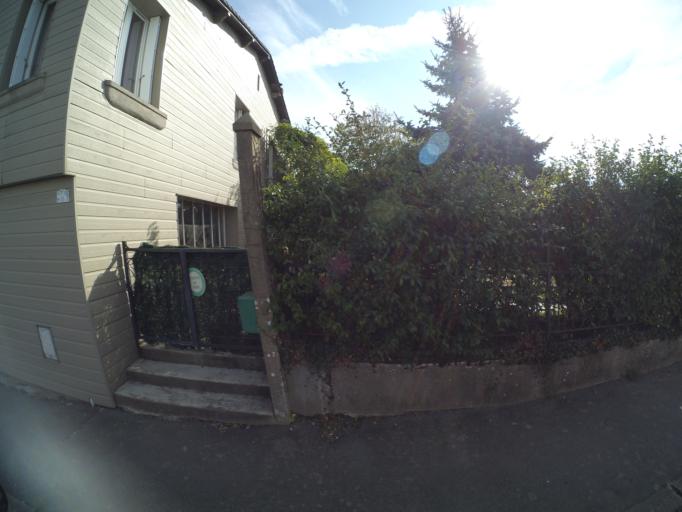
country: FR
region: Pays de la Loire
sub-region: Departement de Maine-et-Loire
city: Tillieres
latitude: 47.1423
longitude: -1.1645
